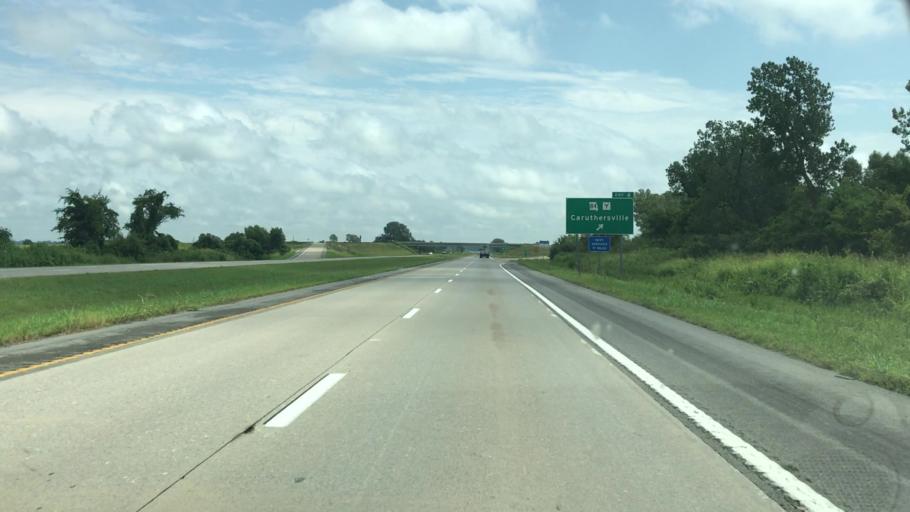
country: US
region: Missouri
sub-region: Pemiscot County
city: Caruthersville
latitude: 36.1539
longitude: -89.6692
